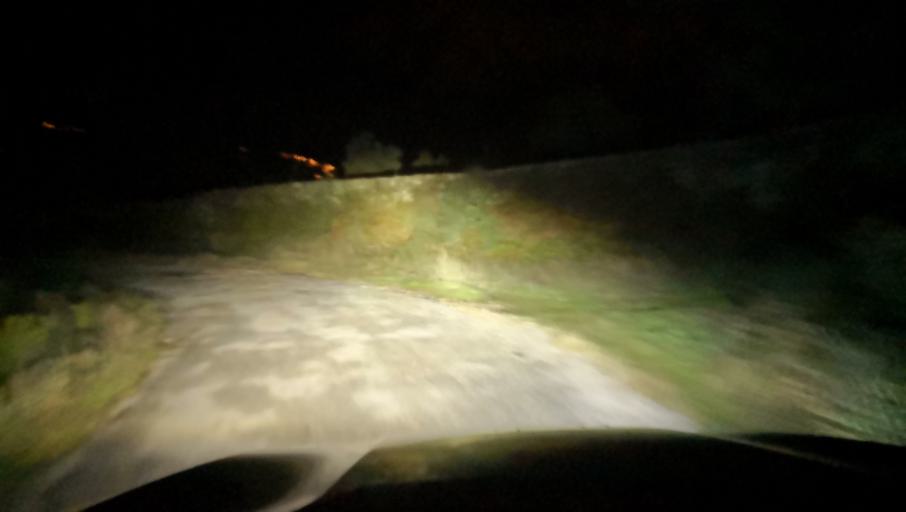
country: PT
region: Vila Real
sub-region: Vila Real
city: Vila Real
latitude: 41.3126
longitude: -7.7467
